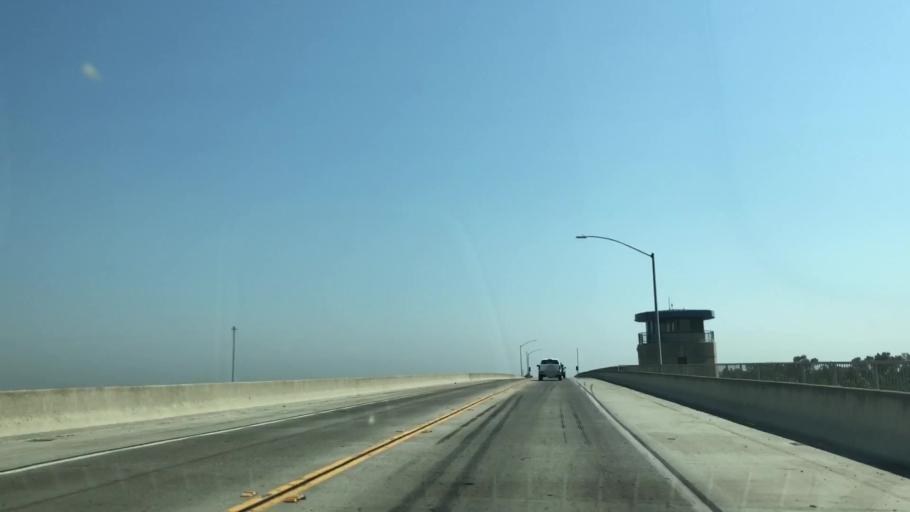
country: US
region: California
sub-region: Sacramento County
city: Walnut Grove
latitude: 38.1149
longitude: -121.4992
